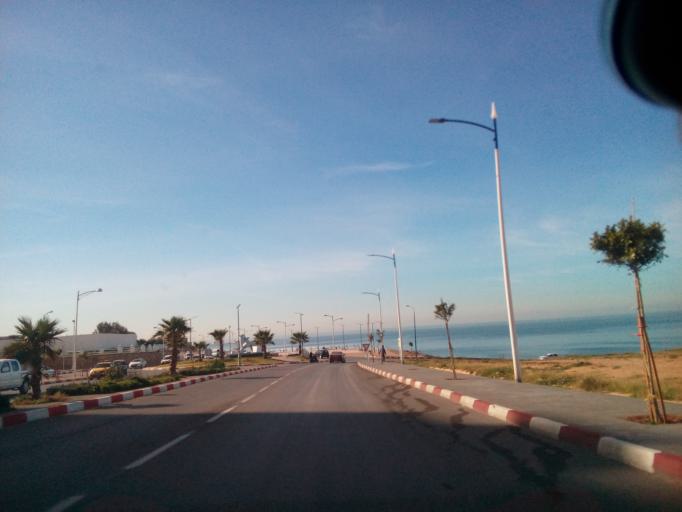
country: DZ
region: Mostaganem
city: Mostaganem
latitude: 35.9442
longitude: 0.0860
